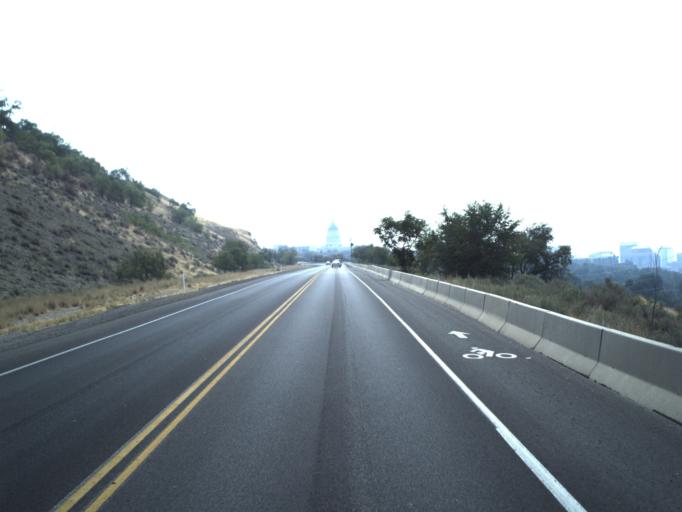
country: US
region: Utah
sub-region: Salt Lake County
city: Salt Lake City
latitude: 40.7894
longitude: -111.8984
